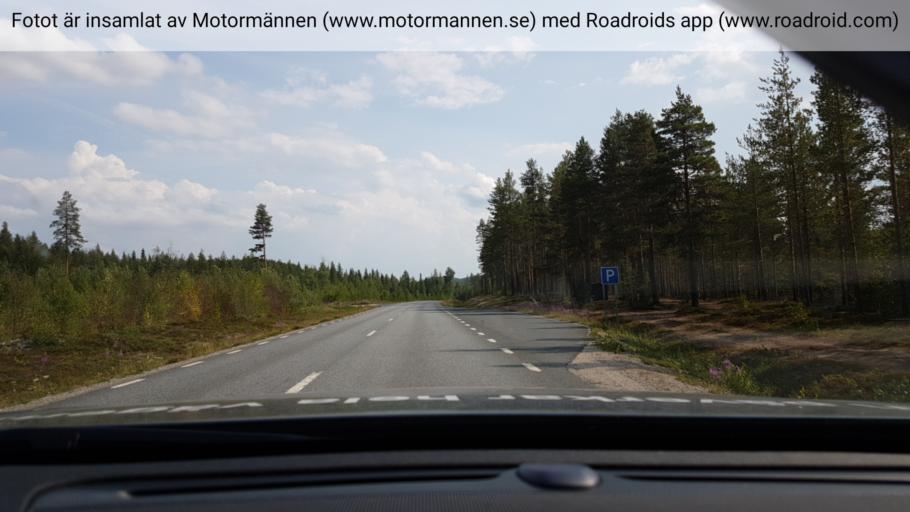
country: SE
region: Vaesterbotten
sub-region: Lycksele Kommun
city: Lycksele
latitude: 64.4123
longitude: 19.0183
